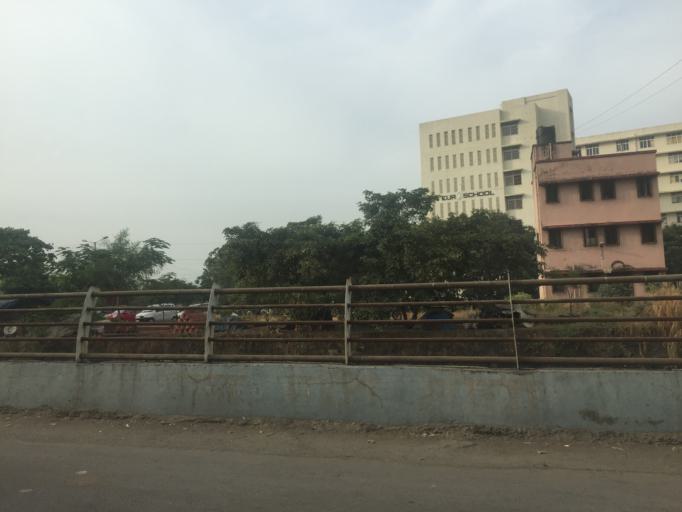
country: IN
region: Maharashtra
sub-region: Thane
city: Airoli
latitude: 19.1555
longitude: 72.9938
